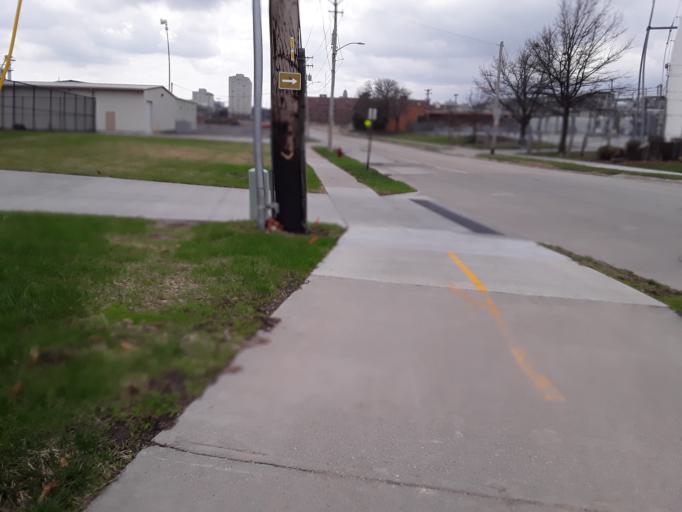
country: US
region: Nebraska
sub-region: Lancaster County
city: Lincoln
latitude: 40.8276
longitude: -96.6964
